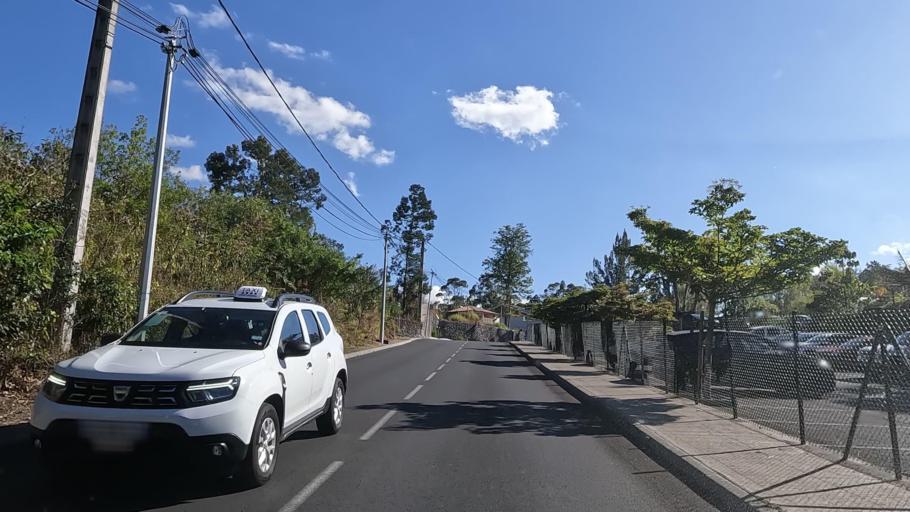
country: RE
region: Reunion
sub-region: Reunion
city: Le Tampon
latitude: -21.2596
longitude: 55.5102
